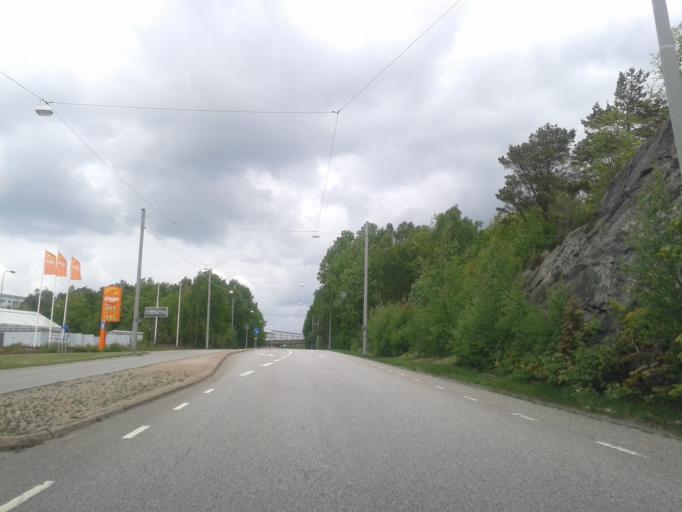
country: SE
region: Vaestra Goetaland
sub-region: Goteborg
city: Gardsten
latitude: 57.8007
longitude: 12.0359
